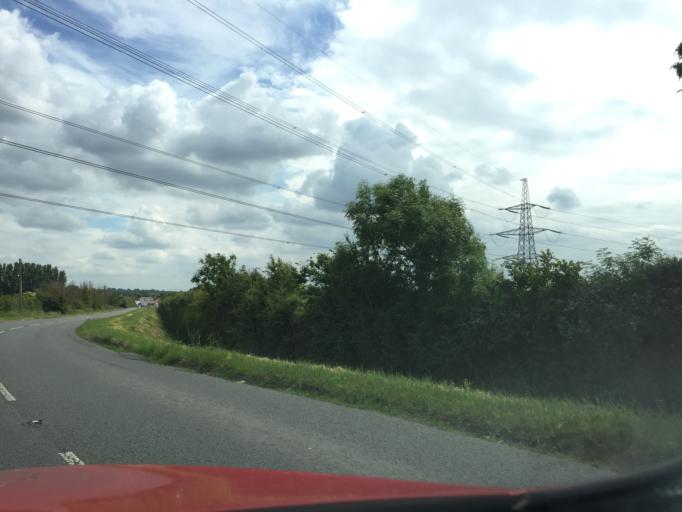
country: GB
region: England
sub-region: South Gloucestershire
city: Severn Beach
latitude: 51.5553
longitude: -2.6345
